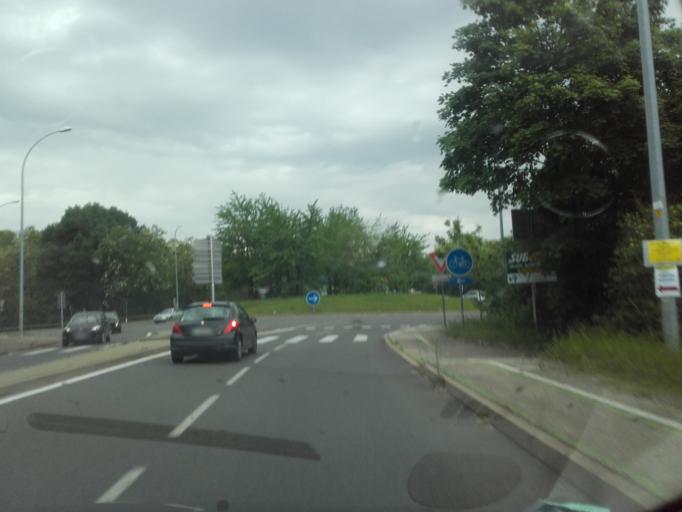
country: FR
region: Rhone-Alpes
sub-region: Departement du Rhone
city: Lissieu
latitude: 45.8443
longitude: 4.7340
